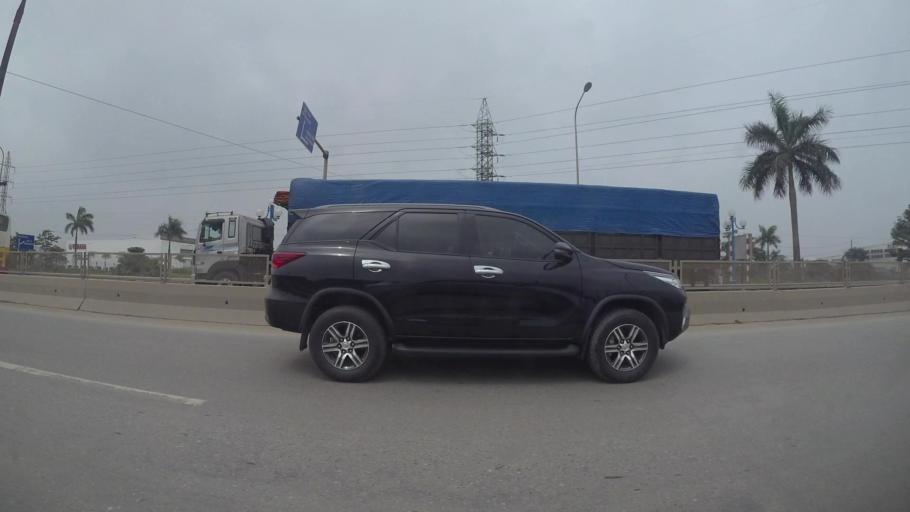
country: VN
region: Ha Noi
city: Tay Ho
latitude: 21.1158
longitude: 105.7846
